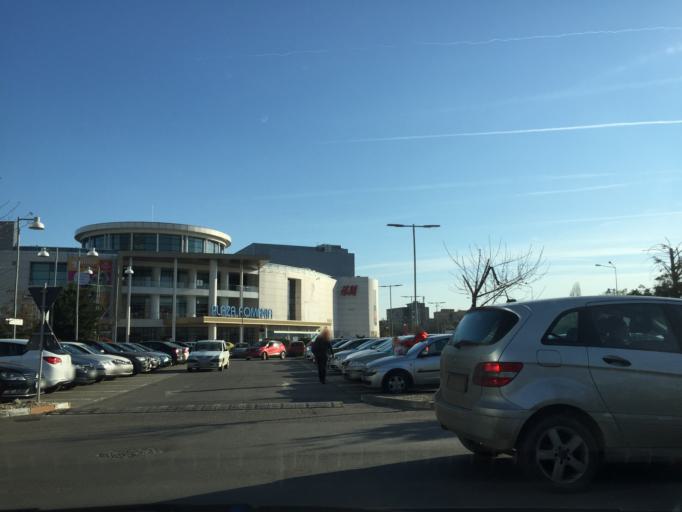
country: RO
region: Ilfov
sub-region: Comuna Chiajna
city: Rosu
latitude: 44.4301
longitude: 26.0348
